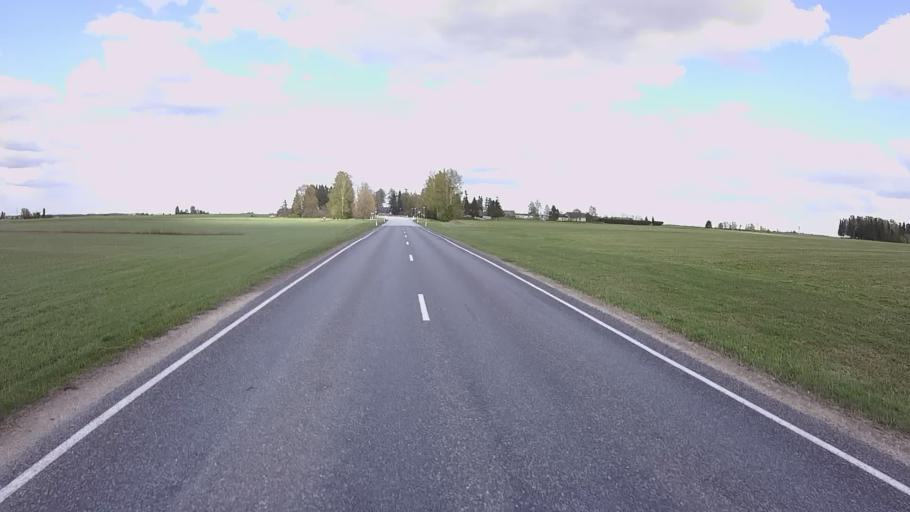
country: EE
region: Jogevamaa
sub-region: Jogeva linn
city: Jogeva
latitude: 58.8050
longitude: 26.5171
